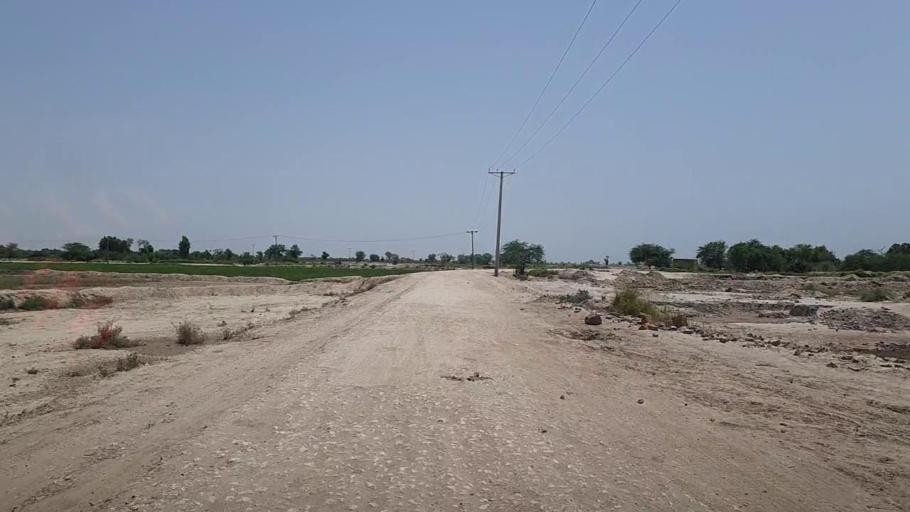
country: PK
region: Sindh
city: Pad Idan
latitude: 26.7688
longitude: 68.2931
